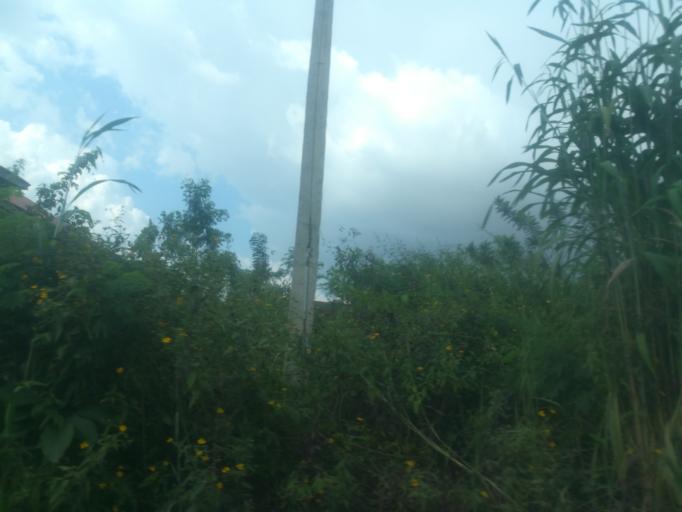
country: NG
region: Oyo
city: Ido
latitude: 7.4118
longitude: 3.8194
